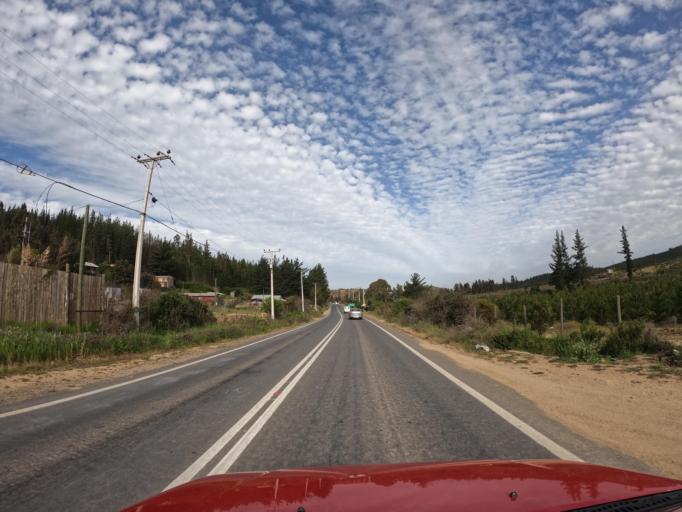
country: CL
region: O'Higgins
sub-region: Provincia de Colchagua
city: Santa Cruz
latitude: -34.3153
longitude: -71.7683
